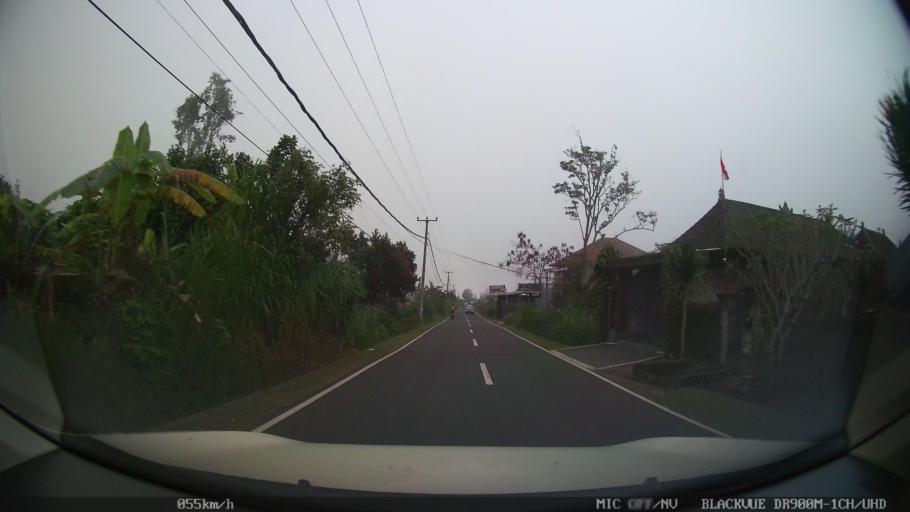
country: ID
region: Bali
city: Banjar Kedisan
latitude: -8.2908
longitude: 115.3174
